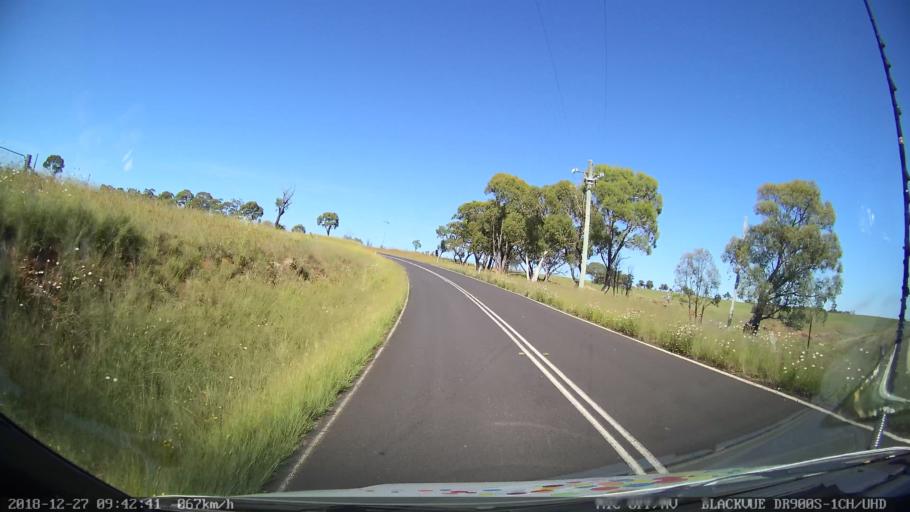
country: AU
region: New South Wales
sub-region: Lithgow
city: Portland
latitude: -33.2999
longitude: 150.0059
